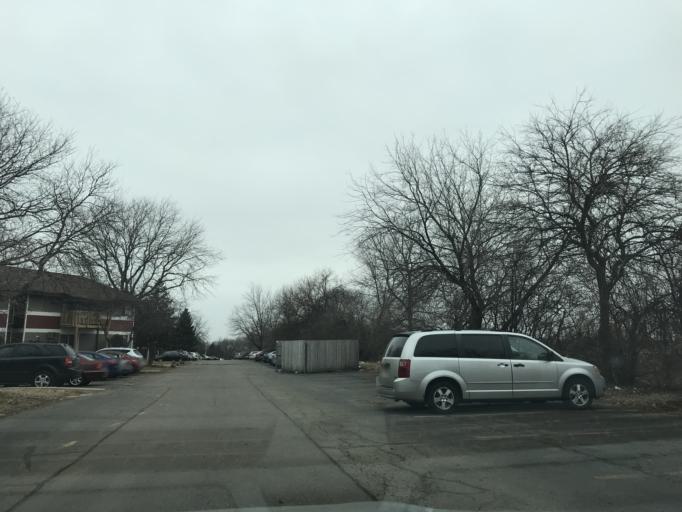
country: US
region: Wisconsin
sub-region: Dane County
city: Monona
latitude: 43.1036
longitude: -89.2958
